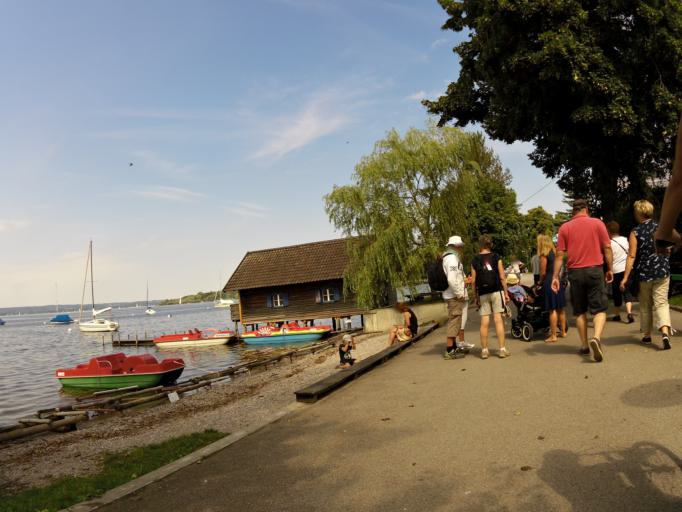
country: DE
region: Bavaria
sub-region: Upper Bavaria
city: Herrsching am Ammersee
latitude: 47.9930
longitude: 11.1703
